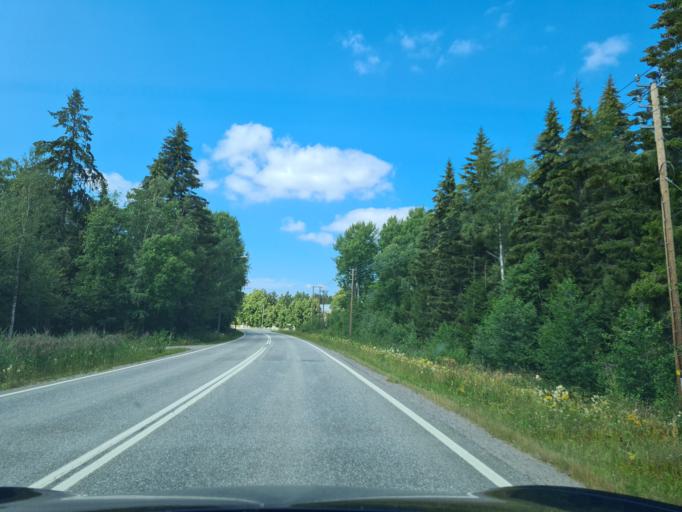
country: FI
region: Ostrobothnia
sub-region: Vaasa
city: Vaasa
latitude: 63.1910
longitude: 21.5630
